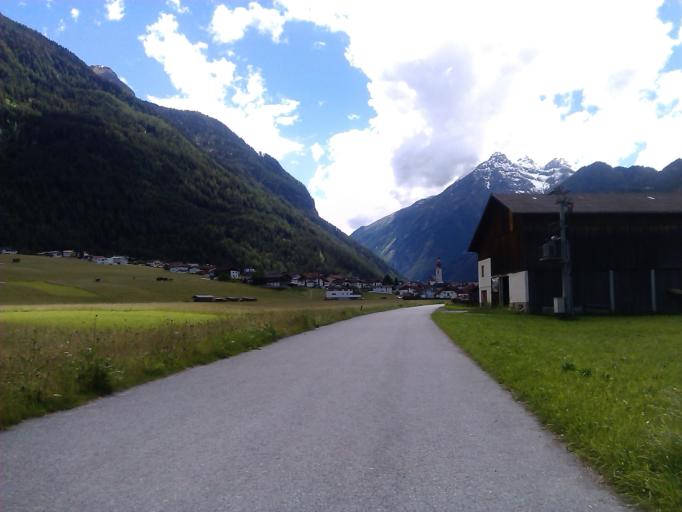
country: AT
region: Tyrol
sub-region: Politischer Bezirk Landeck
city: Pfunds
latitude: 46.9730
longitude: 10.5513
